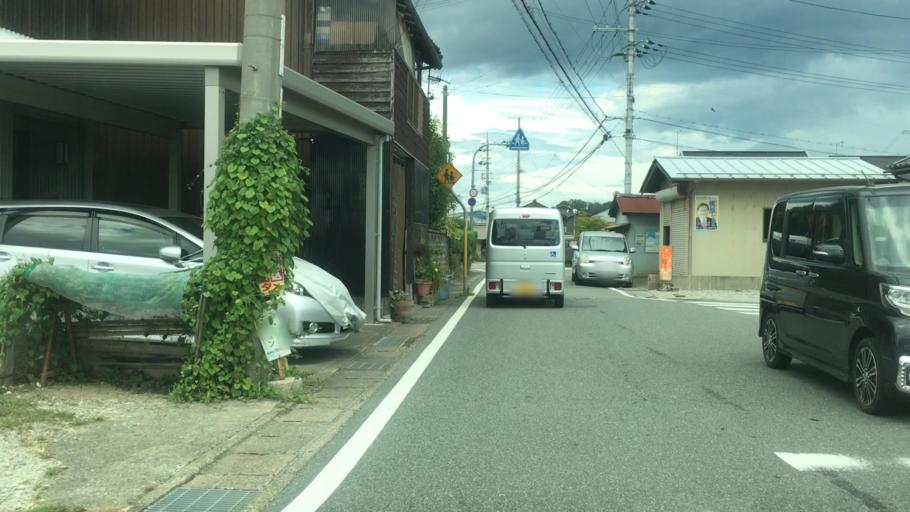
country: JP
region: Hyogo
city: Toyooka
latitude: 35.5284
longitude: 134.8223
